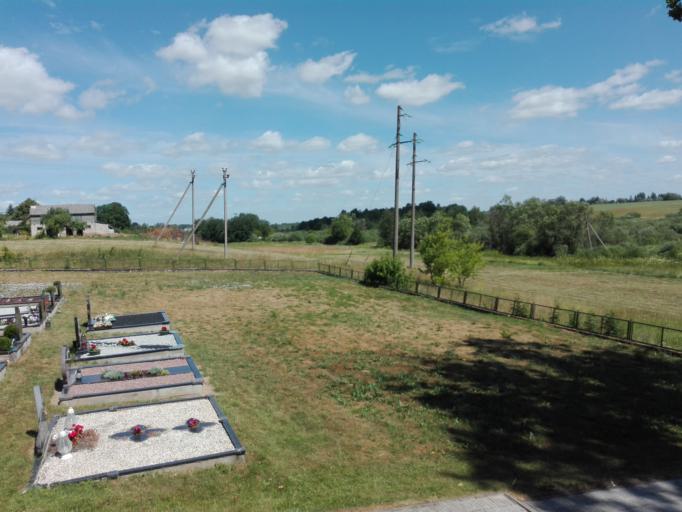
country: LT
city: Kupiskis
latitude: 55.9722
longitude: 25.0034
